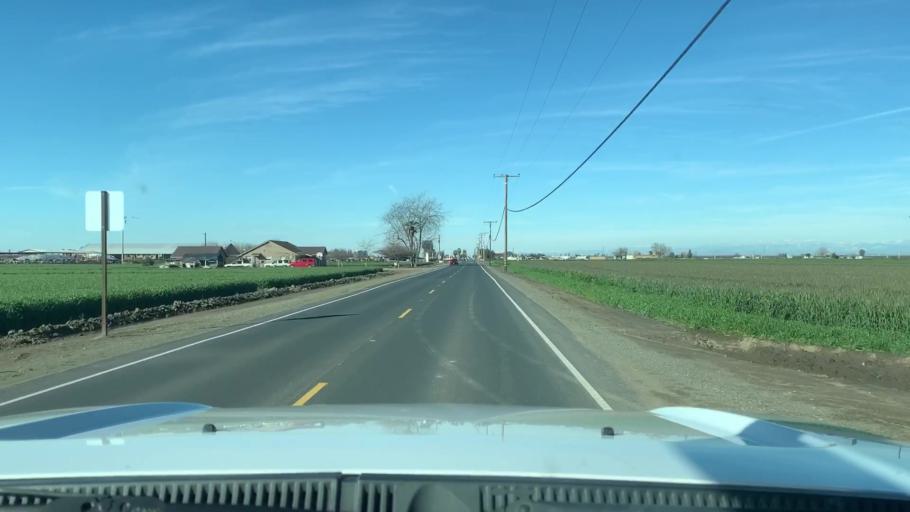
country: US
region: California
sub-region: Kings County
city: Corcoran
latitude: 36.1970
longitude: -119.4931
